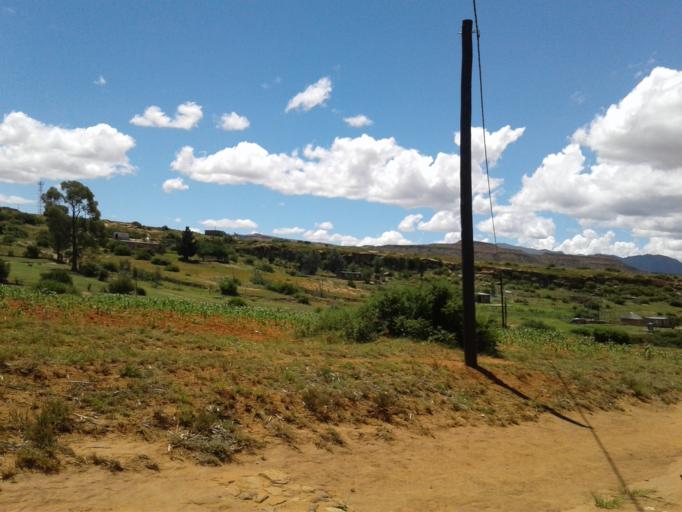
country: LS
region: Quthing
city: Quthing
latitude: -30.3805
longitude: 27.5586
